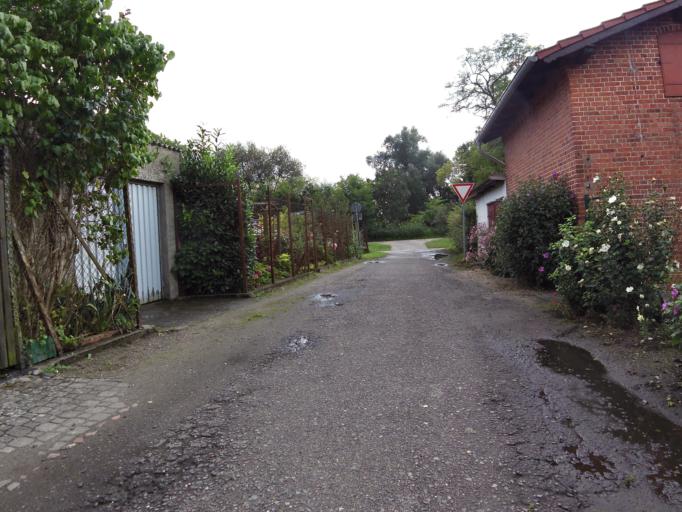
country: DE
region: Saxony-Anhalt
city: Havelberg
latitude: 52.8193
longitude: 12.0678
